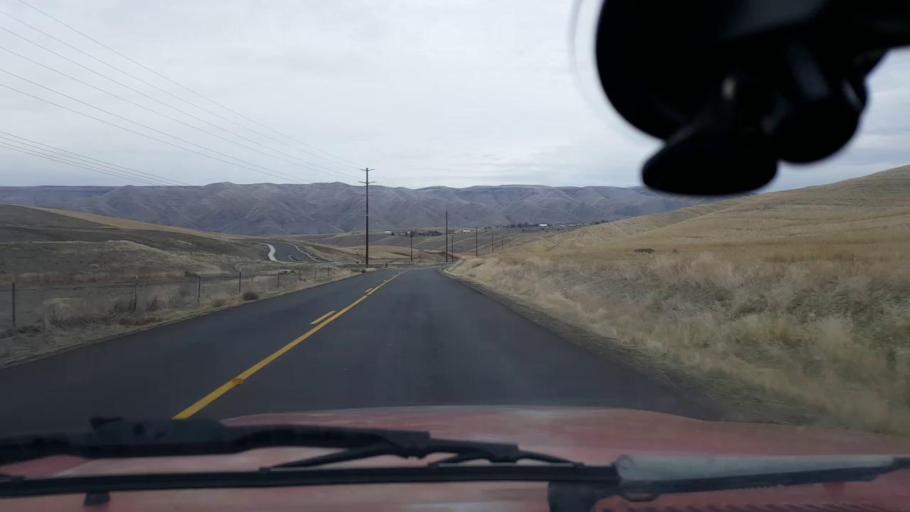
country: US
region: Washington
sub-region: Asotin County
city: Clarkston Heights-Vineland
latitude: 46.3915
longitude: -117.1059
